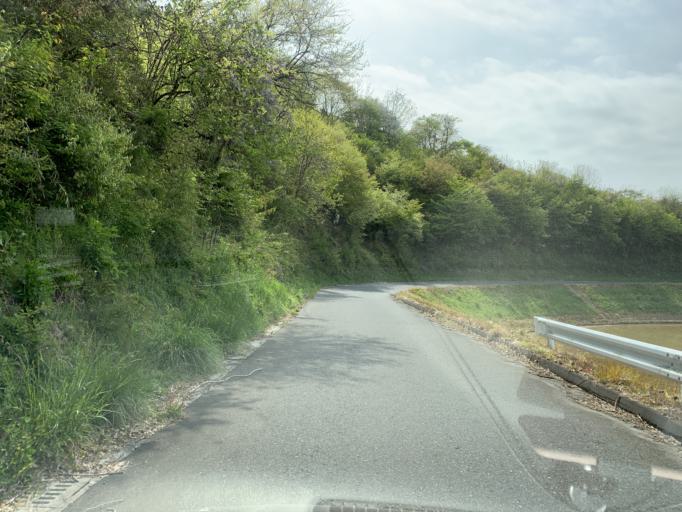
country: JP
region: Iwate
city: Ichinoseki
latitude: 38.9003
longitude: 141.0589
